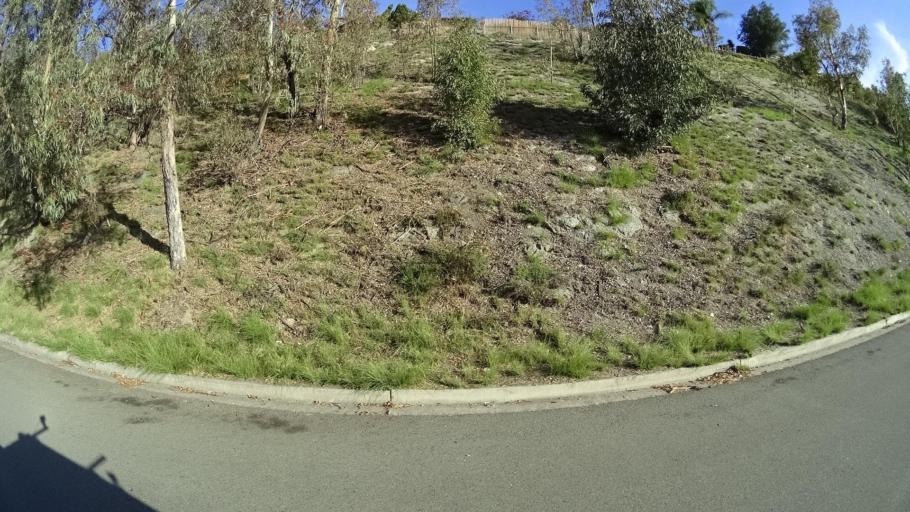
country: US
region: California
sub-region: San Diego County
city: Spring Valley
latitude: 32.7359
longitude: -116.9774
